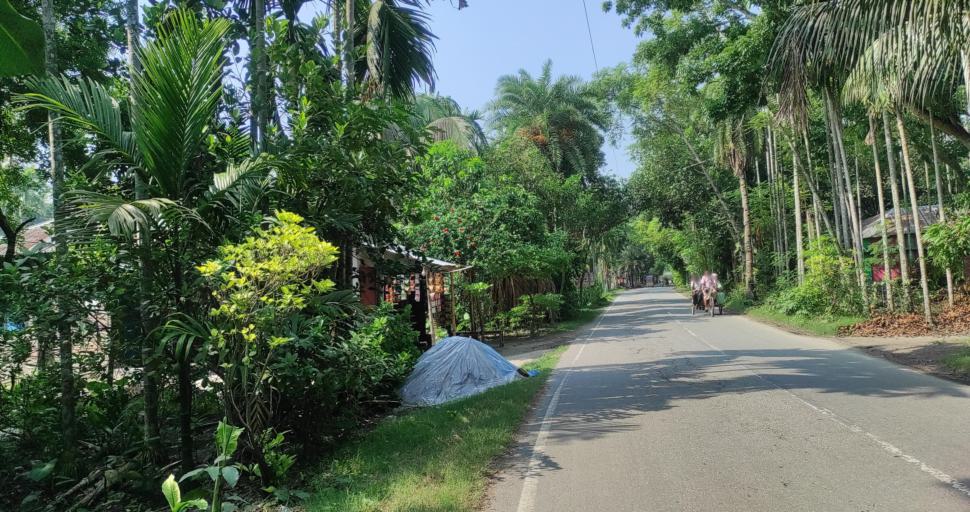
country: BD
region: Rajshahi
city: Ishurdi
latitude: 24.2840
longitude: 89.0652
